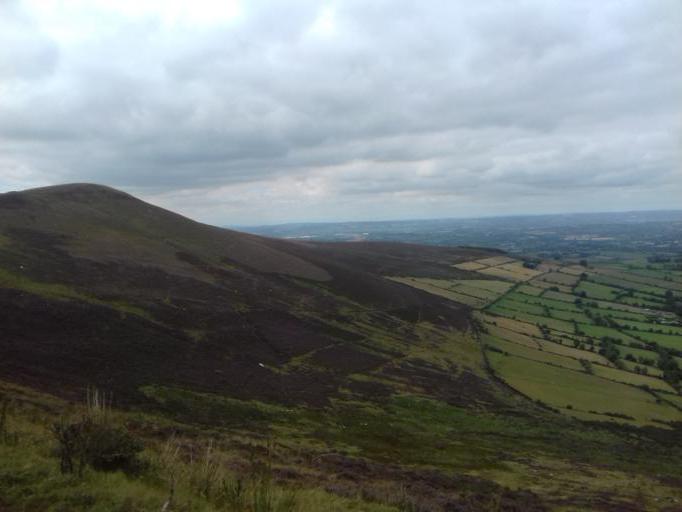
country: IE
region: Leinster
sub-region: Loch Garman
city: Bunclody
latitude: 52.6384
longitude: -6.7876
